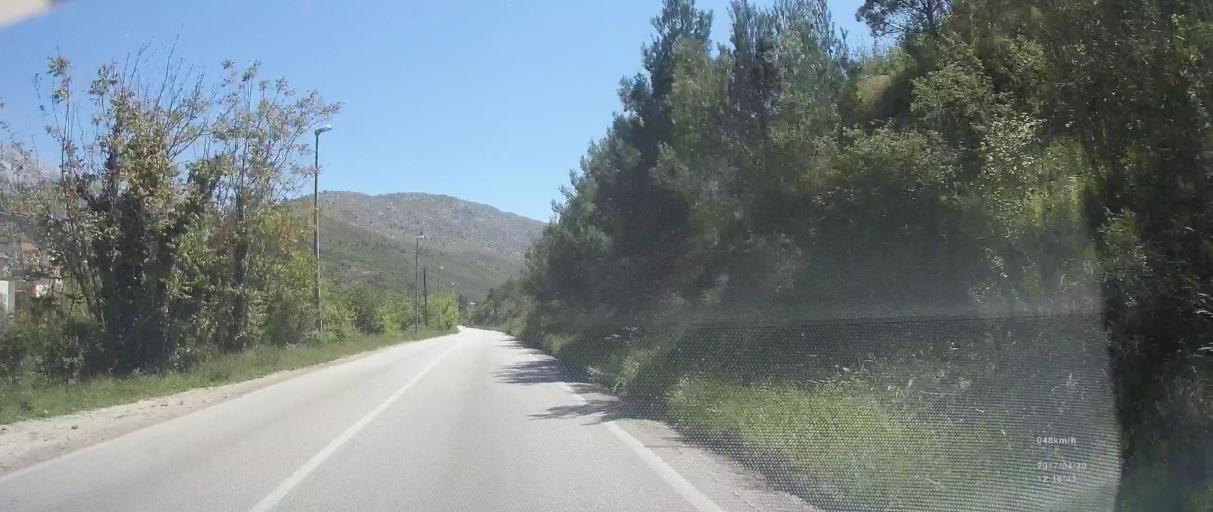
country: HR
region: Splitsko-Dalmatinska
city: Zrnovnica
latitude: 43.5183
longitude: 16.5487
